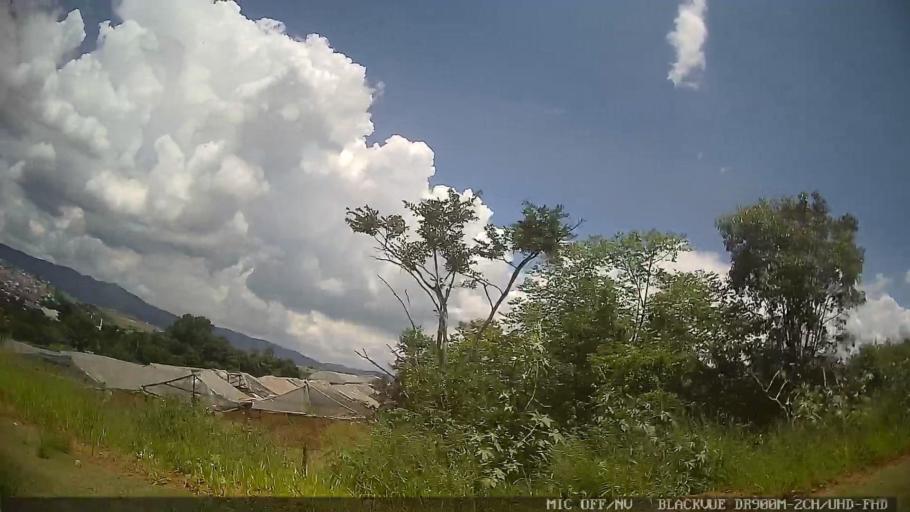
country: BR
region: Sao Paulo
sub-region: Atibaia
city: Atibaia
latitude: -23.1255
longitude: -46.6098
